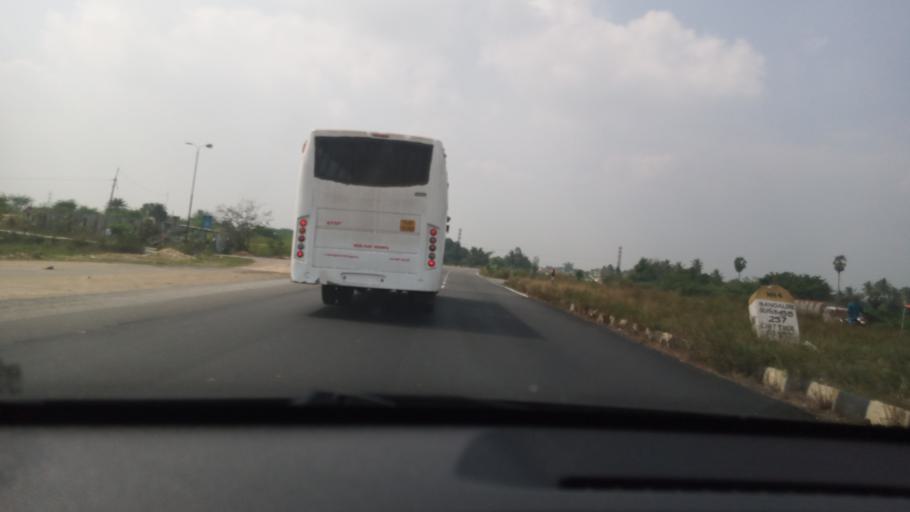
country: IN
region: Tamil Nadu
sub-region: Vellore
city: Walajapet
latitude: 12.8979
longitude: 79.5352
